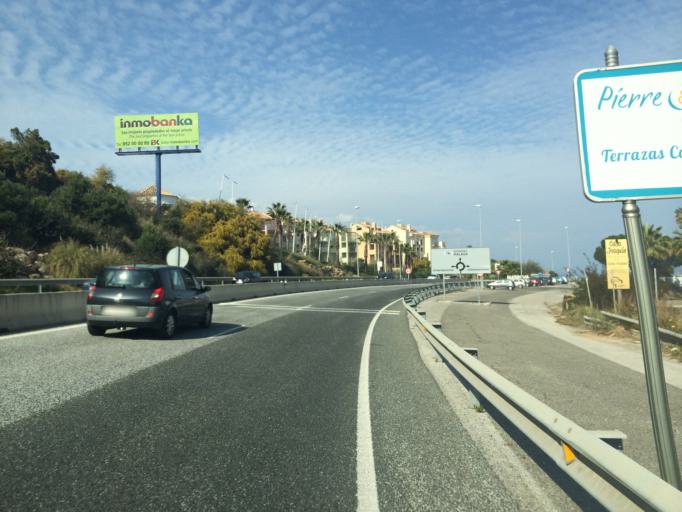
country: ES
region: Andalusia
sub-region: Provincia de Malaga
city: Manilva
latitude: 36.3208
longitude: -5.2459
